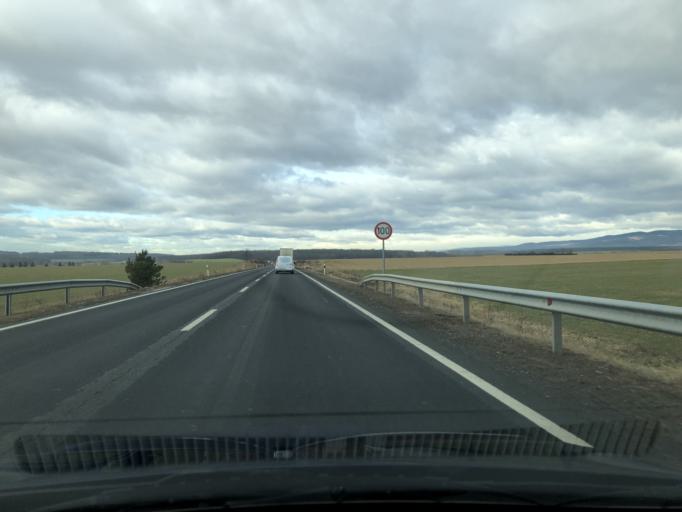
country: AT
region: Burgenland
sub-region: Politischer Bezirk Oberwart
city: Schachendorf
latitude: 47.2460
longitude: 16.5136
